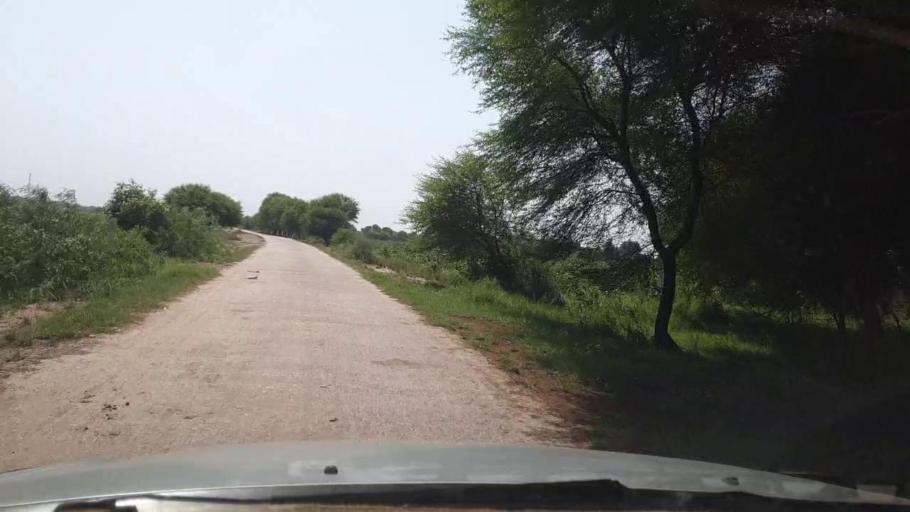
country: PK
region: Sindh
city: Chambar
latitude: 25.2291
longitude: 68.7774
